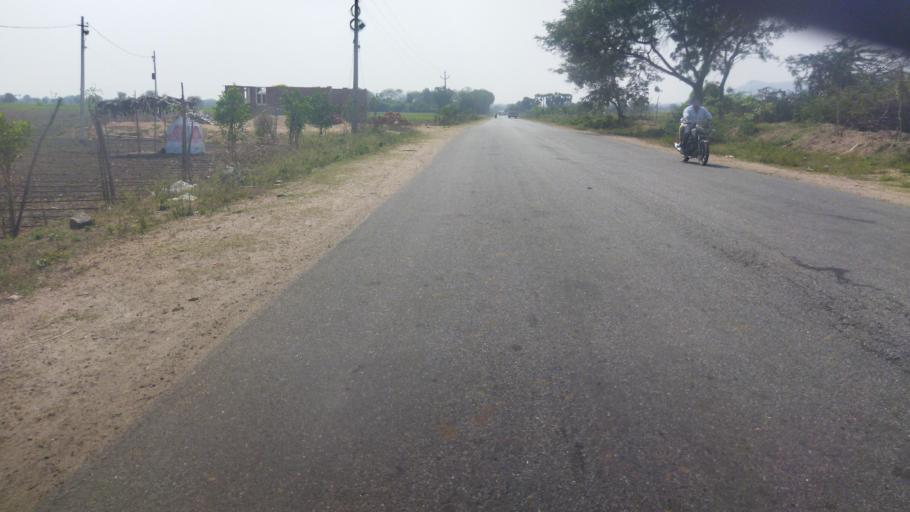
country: IN
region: Telangana
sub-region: Nalgonda
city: Nalgonda
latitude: 17.0933
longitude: 79.2856
